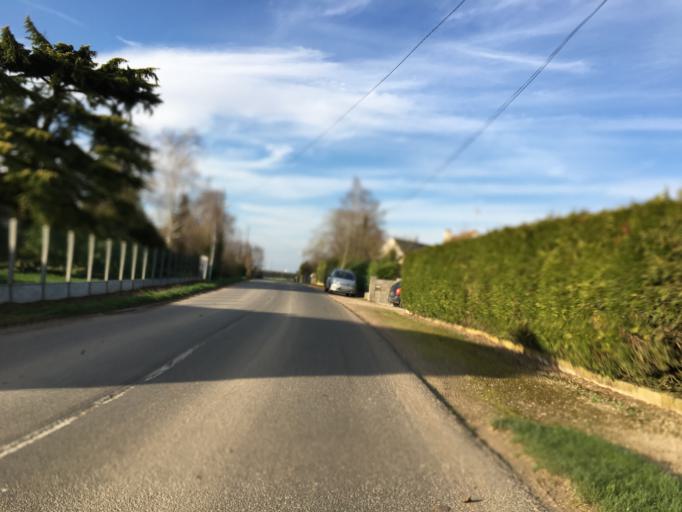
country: FR
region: Centre
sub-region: Departement du Loir-et-Cher
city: Mer
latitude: 47.7544
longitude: 1.5051
